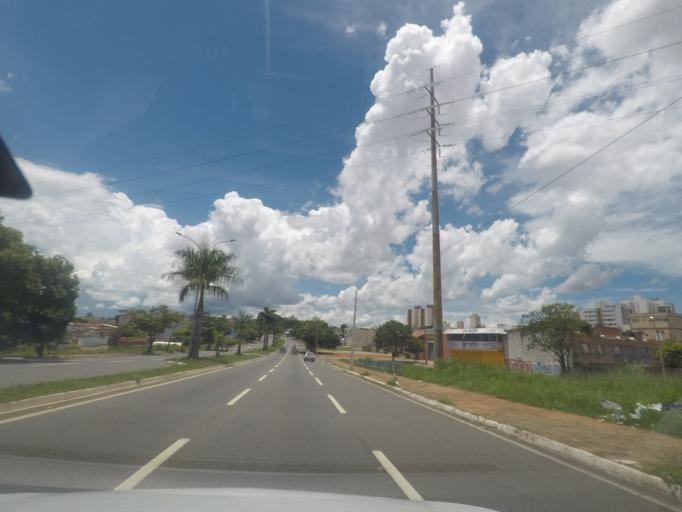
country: BR
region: Goias
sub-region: Goiania
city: Goiania
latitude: -16.6650
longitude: -49.2704
